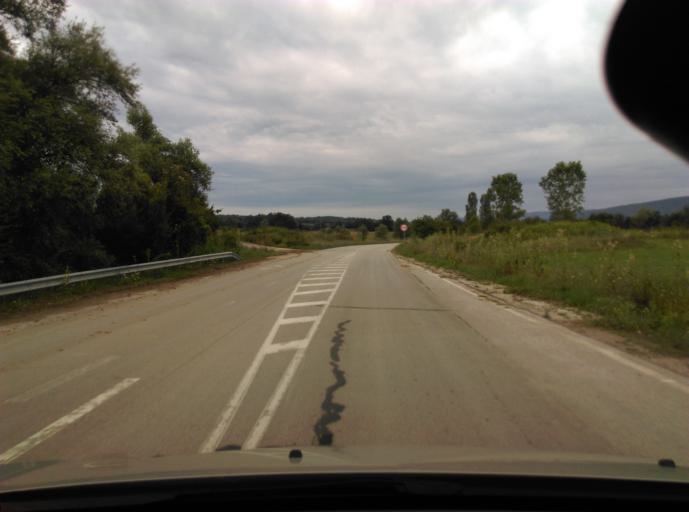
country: BG
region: Lovech
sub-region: Obshtina Ugurchin
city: Ugurchin
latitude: 43.0820
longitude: 24.4456
